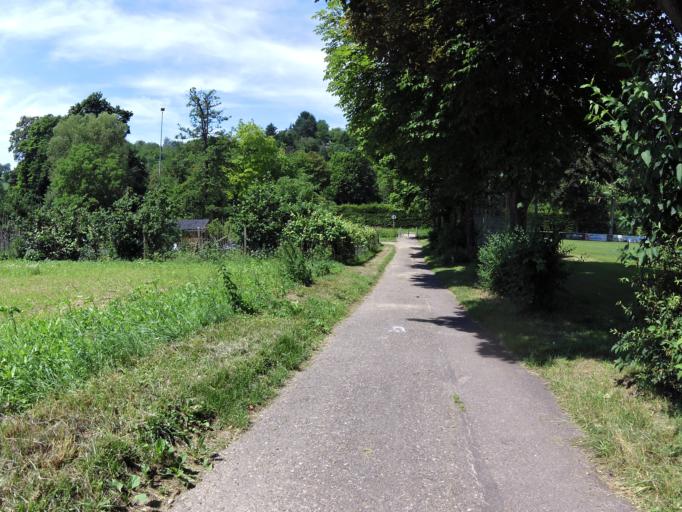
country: DE
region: Baden-Wuerttemberg
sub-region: Freiburg Region
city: Lahr
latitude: 48.3291
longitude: 7.8620
